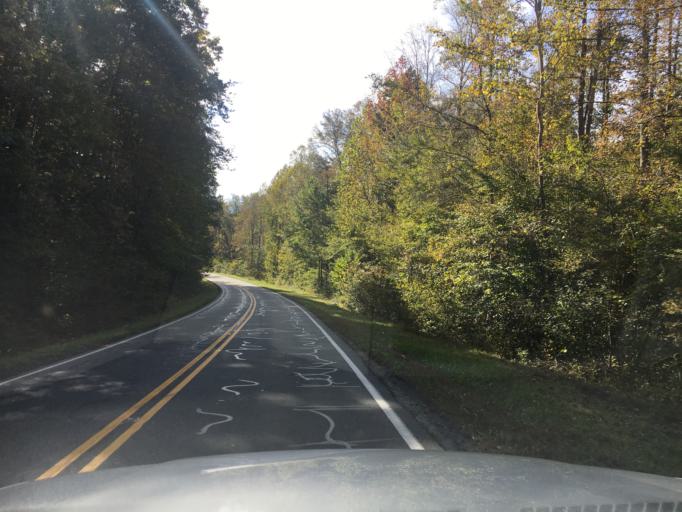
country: US
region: North Carolina
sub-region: Rutherford County
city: Spindale
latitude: 35.3461
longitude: -81.9470
